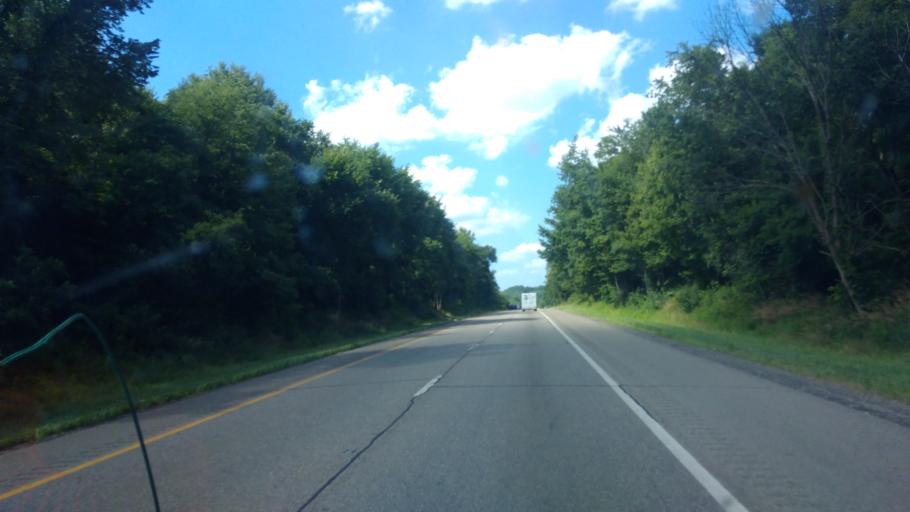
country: US
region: Ohio
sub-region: Stark County
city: Richville
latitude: 40.6689
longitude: -81.4366
